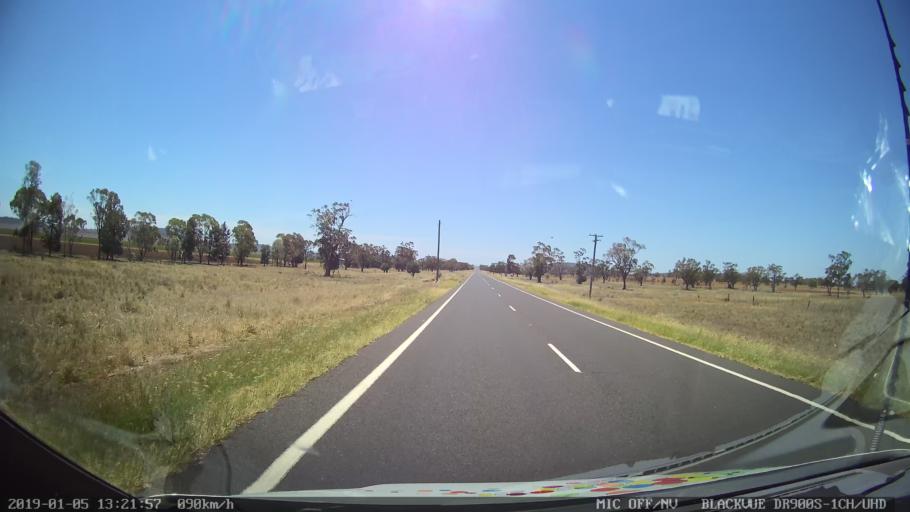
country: AU
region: New South Wales
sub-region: Gunnedah
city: Gunnedah
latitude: -31.0902
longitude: 149.9554
